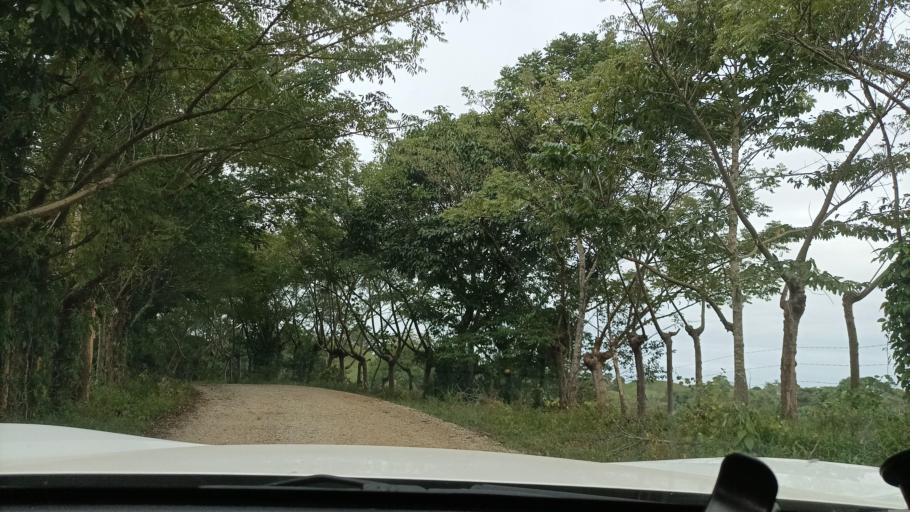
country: MX
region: Veracruz
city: Hidalgotitlan
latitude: 17.5938
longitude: -94.4215
